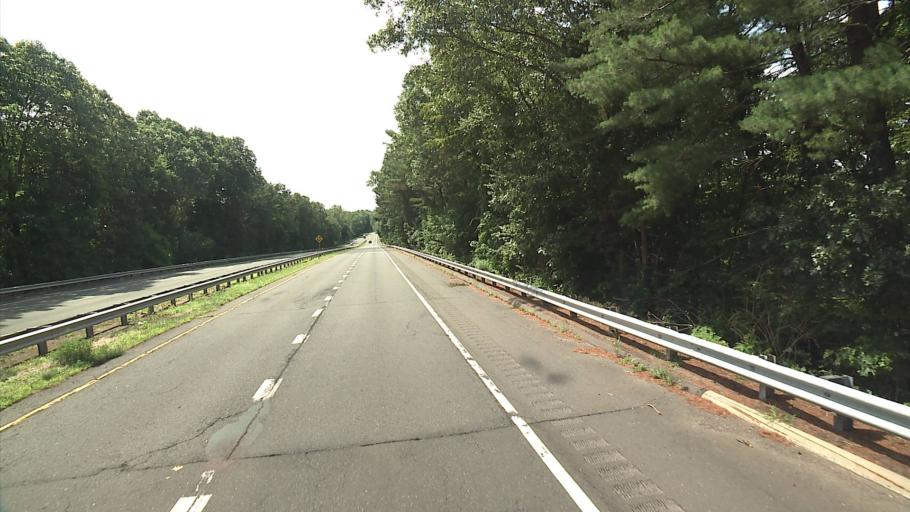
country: US
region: Connecticut
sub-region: Hartford County
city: Glastonbury Center
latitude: 41.7013
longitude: -72.6008
